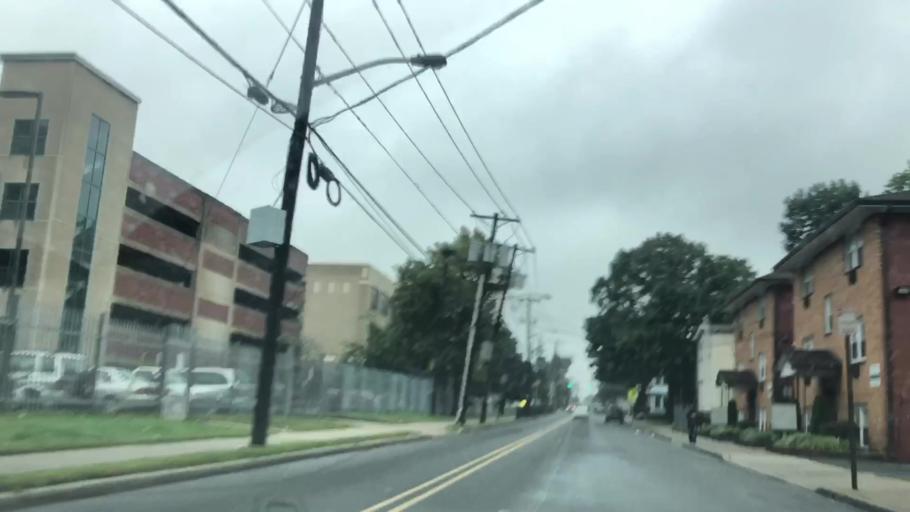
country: US
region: New Jersey
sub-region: Essex County
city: Irvington
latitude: 40.7300
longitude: -74.2195
